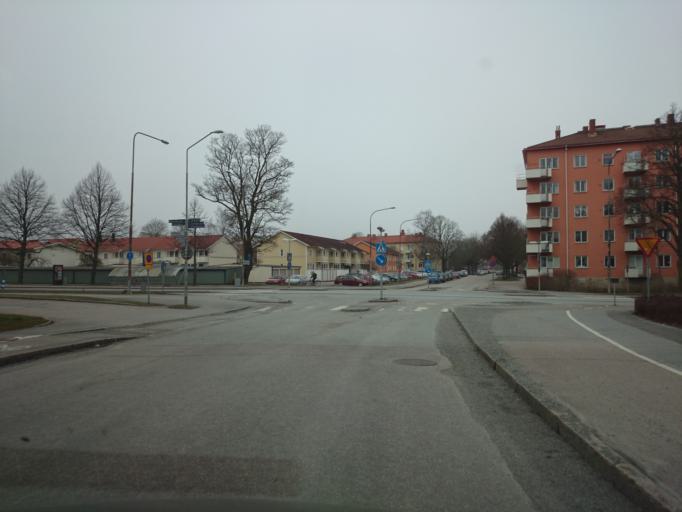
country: SE
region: Uppsala
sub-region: Uppsala Kommun
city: Uppsala
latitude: 59.8587
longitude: 17.6158
